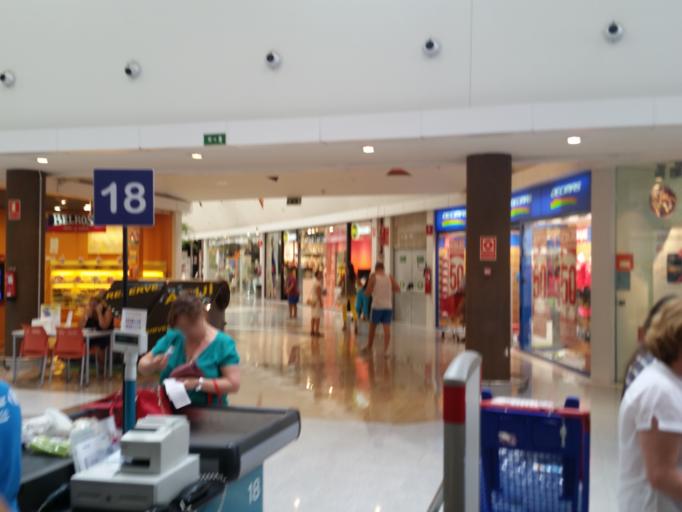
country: ES
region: Andalusia
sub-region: Provincia de Malaga
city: Torremolinos
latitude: 36.6123
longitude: -4.5126
